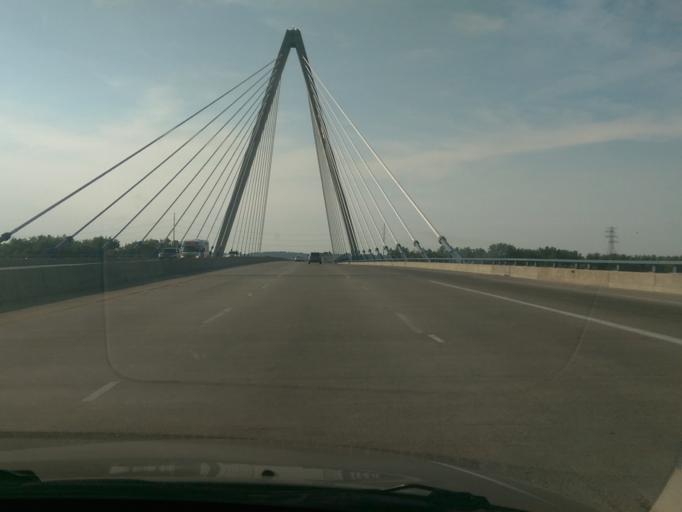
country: US
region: Missouri
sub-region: Clay County
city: North Kansas City
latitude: 39.1211
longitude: -94.5648
